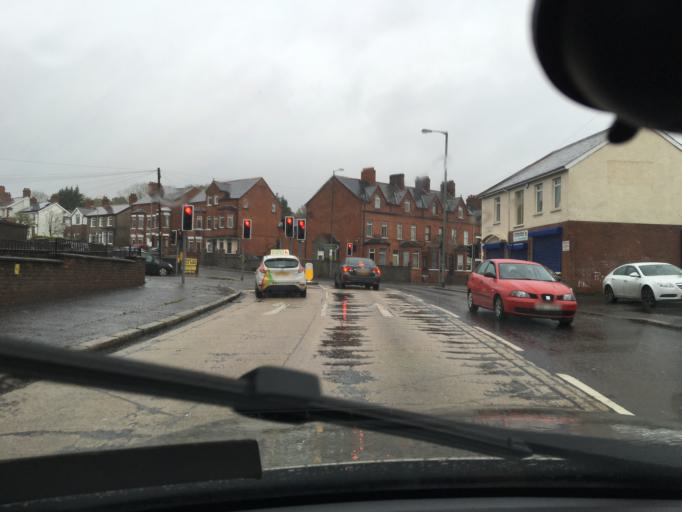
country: GB
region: Northern Ireland
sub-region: City of Belfast
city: Belfast
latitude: 54.6079
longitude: -5.9734
